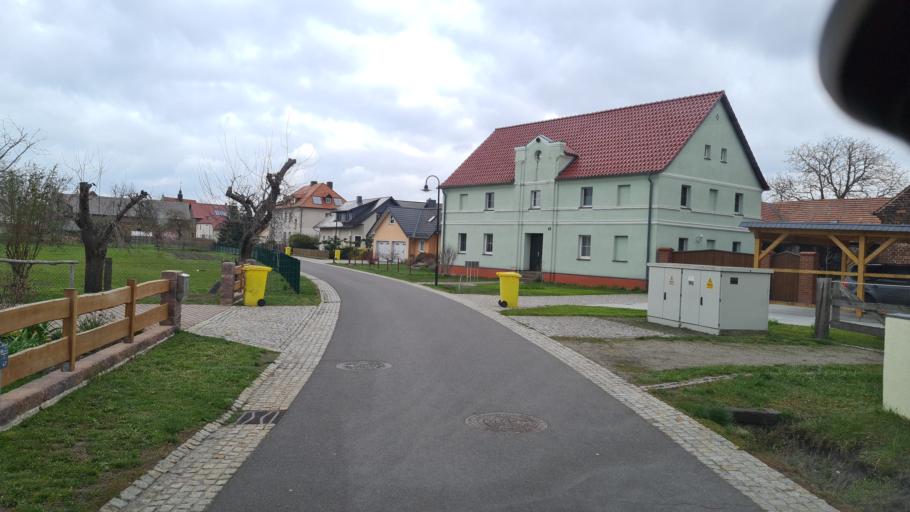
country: DE
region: Brandenburg
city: Hohenbocka
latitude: 51.4614
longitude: 14.0697
